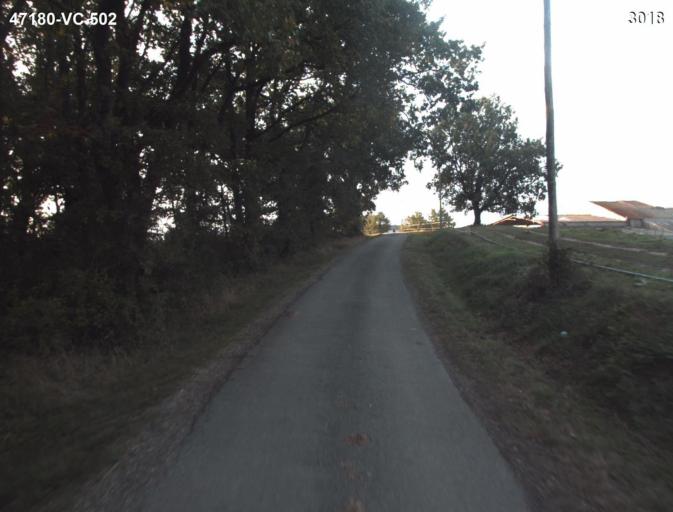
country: FR
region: Aquitaine
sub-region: Departement du Lot-et-Garonne
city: Sainte-Colombe-en-Bruilhois
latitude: 44.1838
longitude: 0.4827
